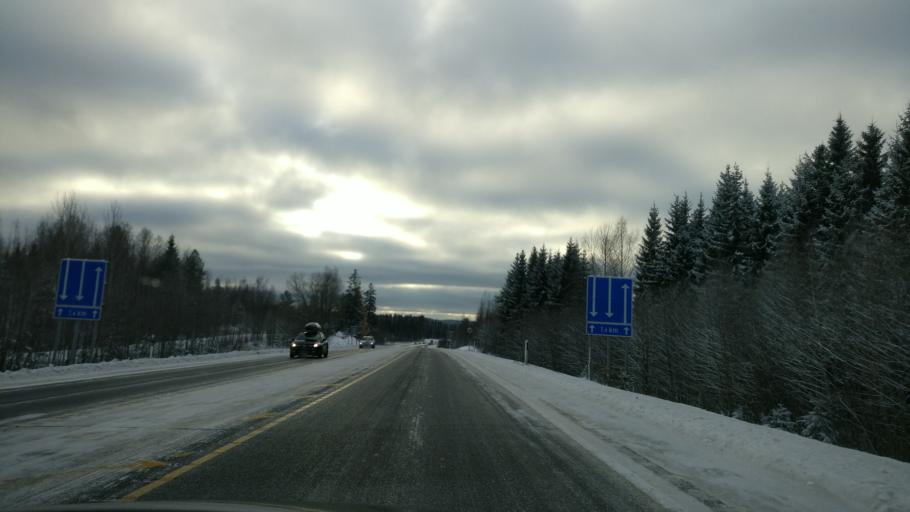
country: FI
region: Southern Savonia
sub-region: Mikkeli
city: Pertunmaa
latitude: 61.3795
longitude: 26.3032
